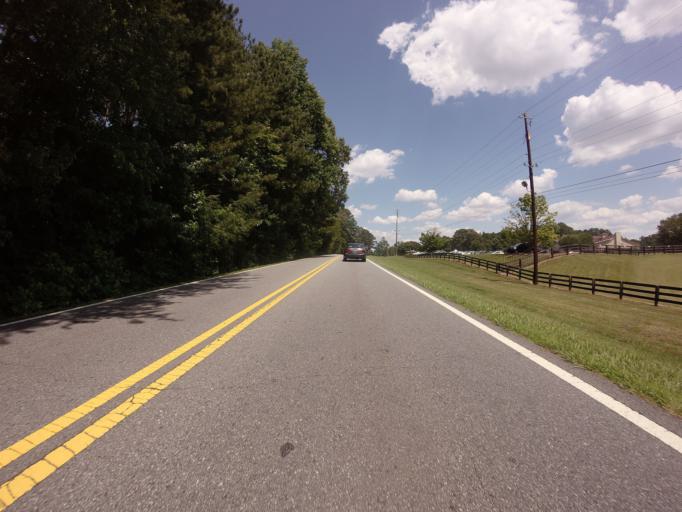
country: US
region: Georgia
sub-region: Fulton County
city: Johns Creek
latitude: 34.0136
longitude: -84.2250
